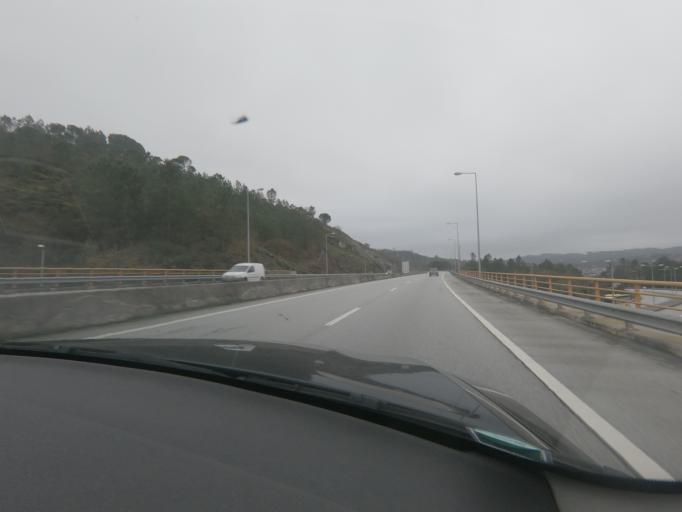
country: PT
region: Viseu
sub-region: Viseu
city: Viseu
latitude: 40.6127
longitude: -7.9650
